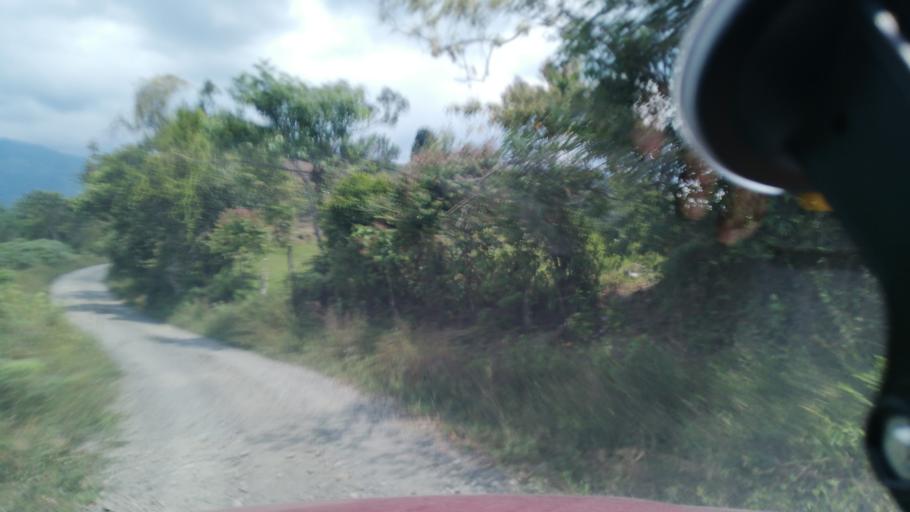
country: CO
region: Cundinamarca
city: Vergara
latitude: 5.1872
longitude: -74.2732
